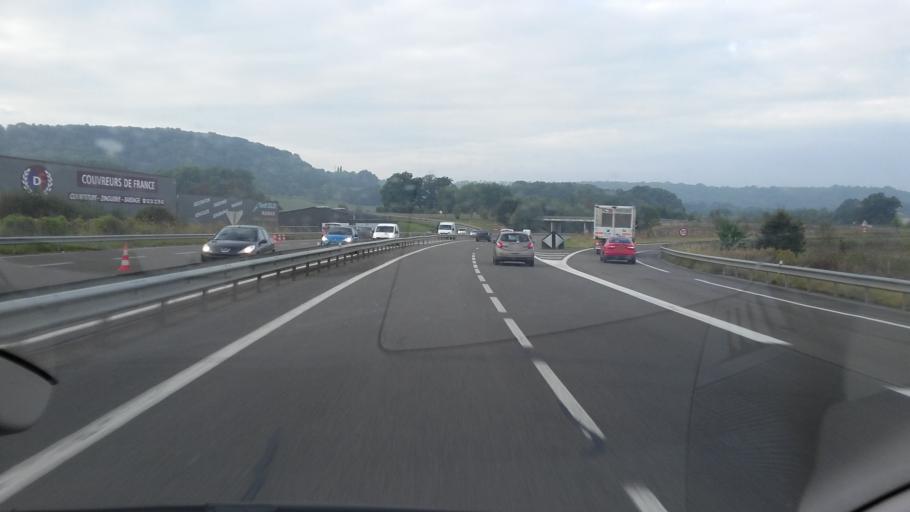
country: FR
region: Champagne-Ardenne
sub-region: Departement des Ardennes
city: La Francheville
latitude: 49.6450
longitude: 4.6294
